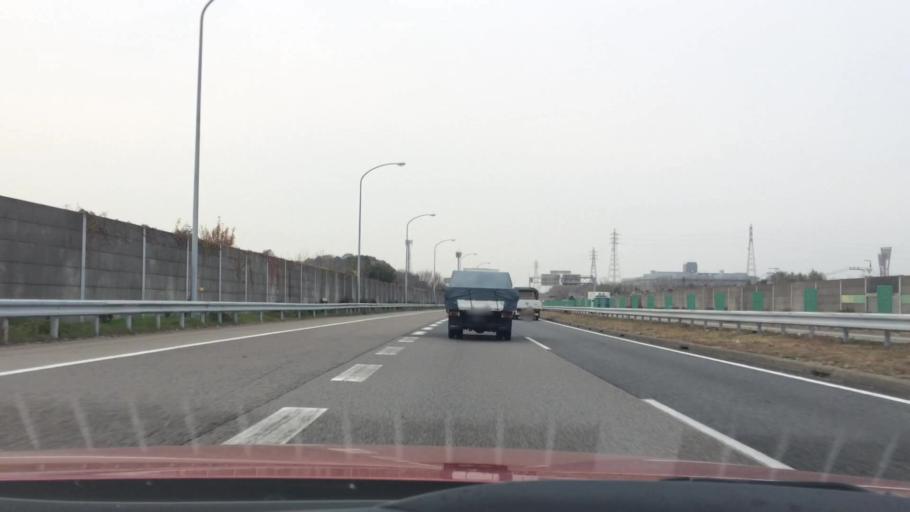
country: JP
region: Aichi
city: Kasugai
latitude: 35.2866
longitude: 136.9708
